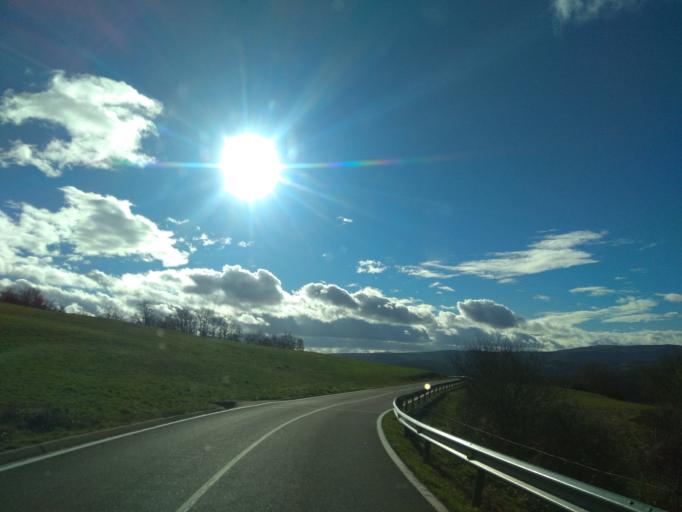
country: ES
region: Cantabria
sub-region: Provincia de Cantabria
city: San Martin de Elines
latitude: 42.9168
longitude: -3.8659
